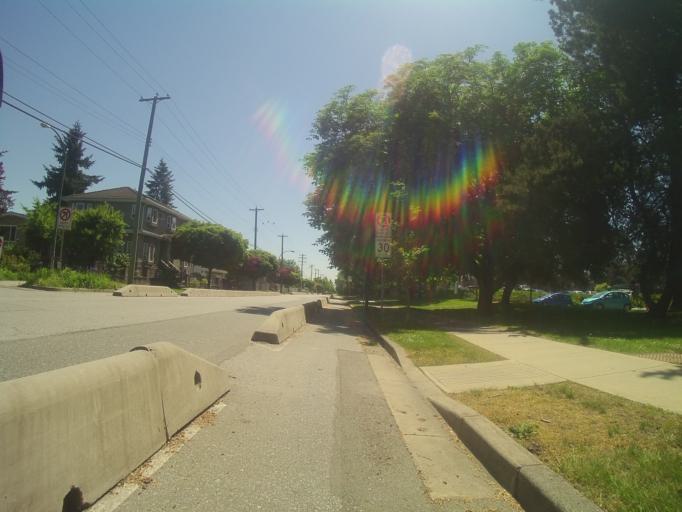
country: CA
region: British Columbia
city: Vancouver
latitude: 49.2250
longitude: -123.1061
